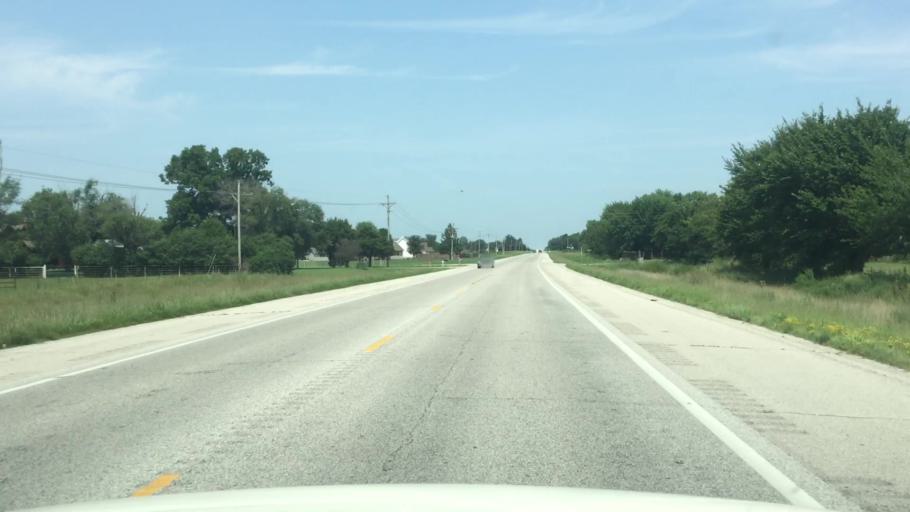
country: US
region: Kansas
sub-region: Cherokee County
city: Galena
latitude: 37.0921
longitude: -94.7044
